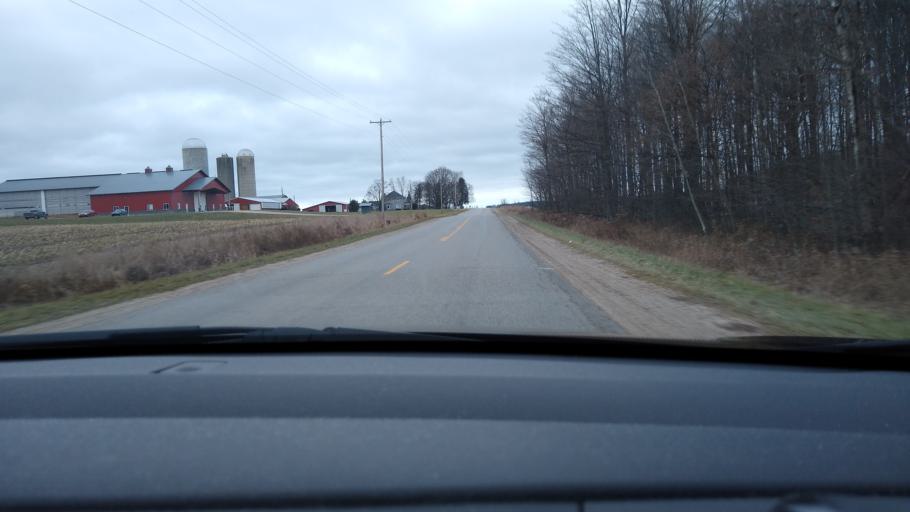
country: US
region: Michigan
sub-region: Missaukee County
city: Lake City
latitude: 44.2960
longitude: -85.0543
